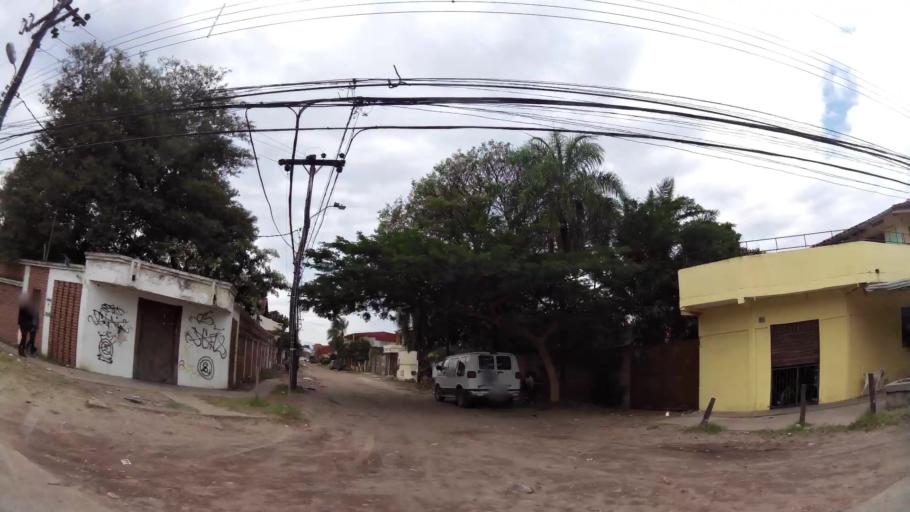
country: BO
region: Santa Cruz
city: Santa Cruz de la Sierra
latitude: -17.7430
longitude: -63.1766
